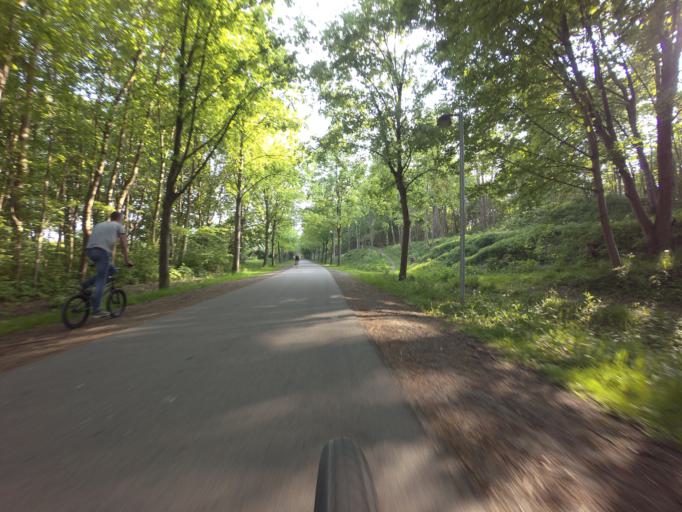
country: DK
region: Capital Region
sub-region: Rodovre Kommune
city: Rodovre
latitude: 55.6835
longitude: 12.4323
